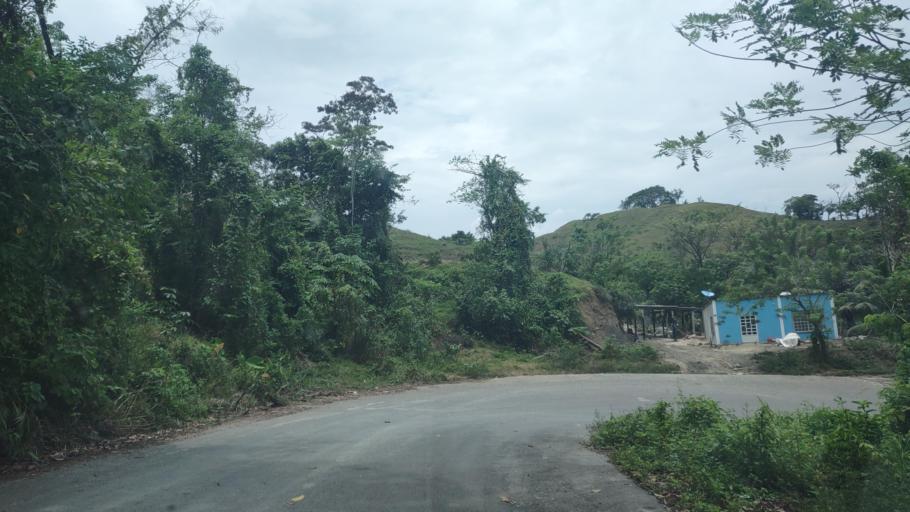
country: MX
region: Tabasco
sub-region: Huimanguillo
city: Francisco Rueda
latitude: 17.5248
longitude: -94.1385
